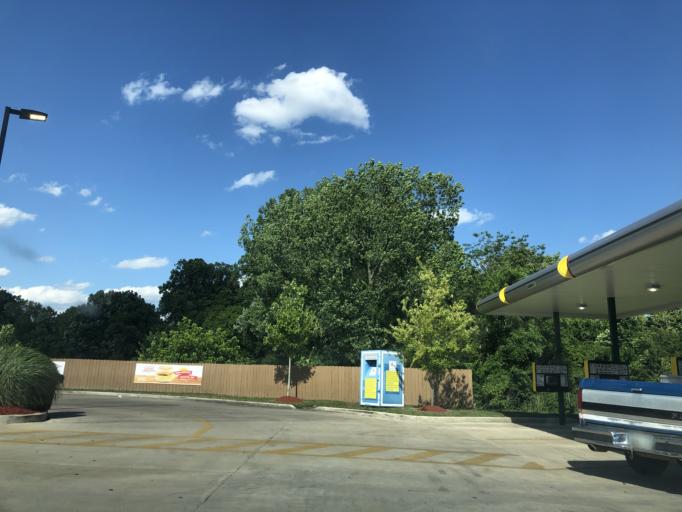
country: US
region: Tennessee
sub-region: Davidson County
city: Belle Meade
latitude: 36.0461
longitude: -86.9502
